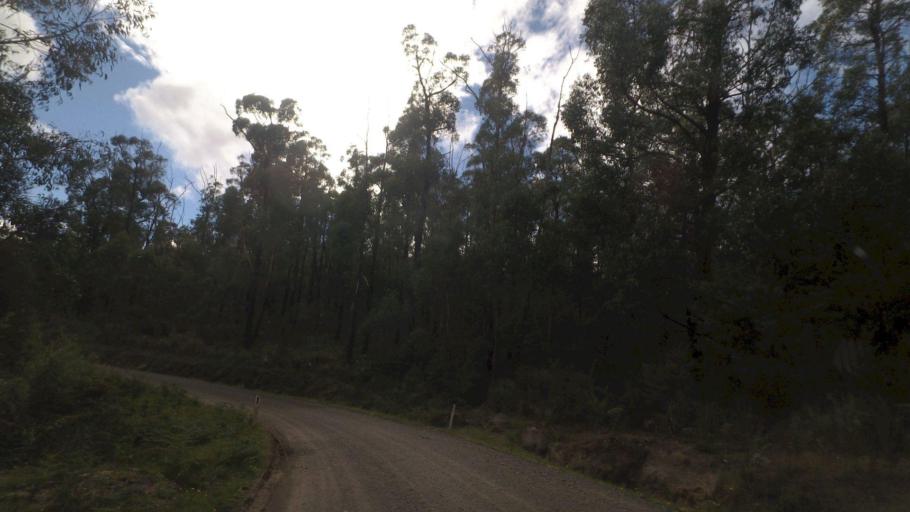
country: AU
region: Victoria
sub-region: Cardinia
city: Bunyip
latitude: -38.0014
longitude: 145.8125
